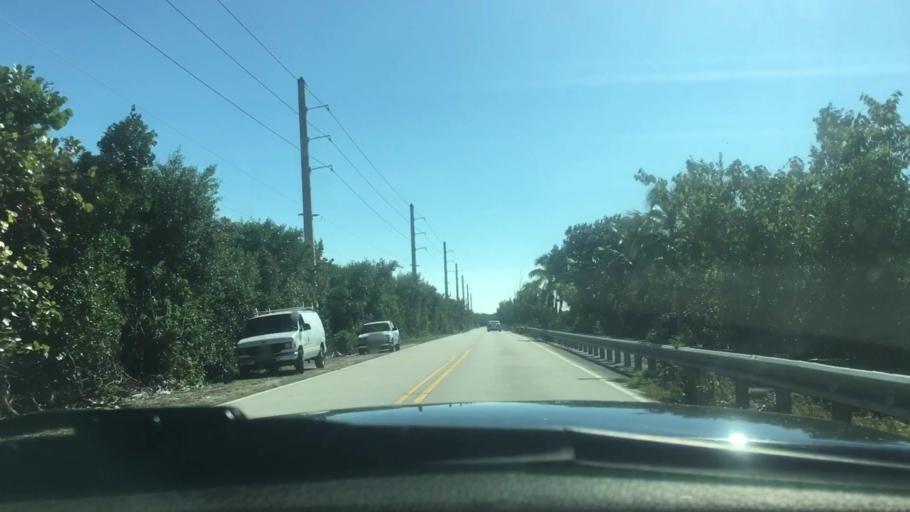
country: US
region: Florida
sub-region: Monroe County
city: North Key Largo
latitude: 25.2963
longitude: -80.3851
